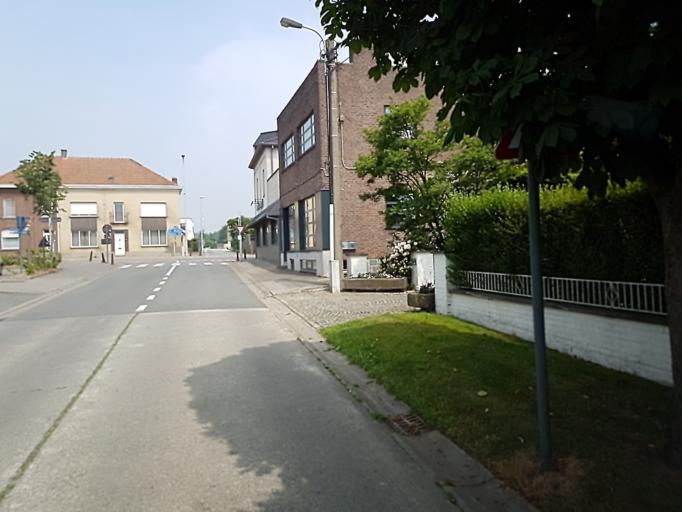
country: BE
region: Flanders
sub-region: Provincie Oost-Vlaanderen
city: Sint-Maria-Lierde
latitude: 50.8207
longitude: 3.8914
